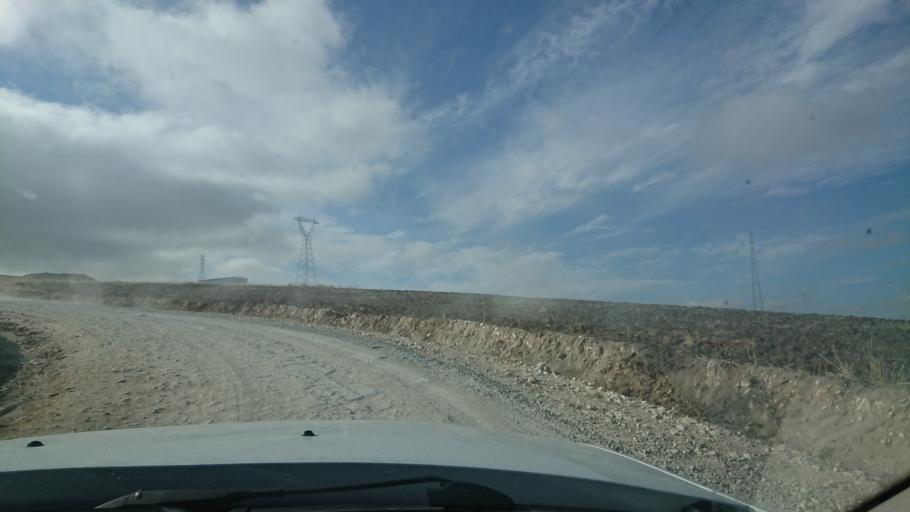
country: TR
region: Aksaray
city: Agacoren
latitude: 38.8494
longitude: 33.9467
